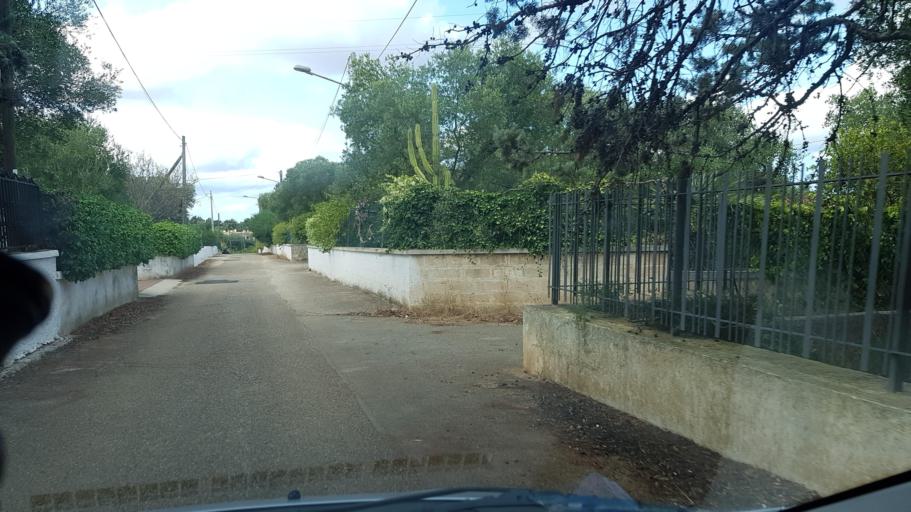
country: IT
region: Apulia
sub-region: Provincia di Brindisi
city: San Vito dei Normanni
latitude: 40.6661
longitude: 17.7218
